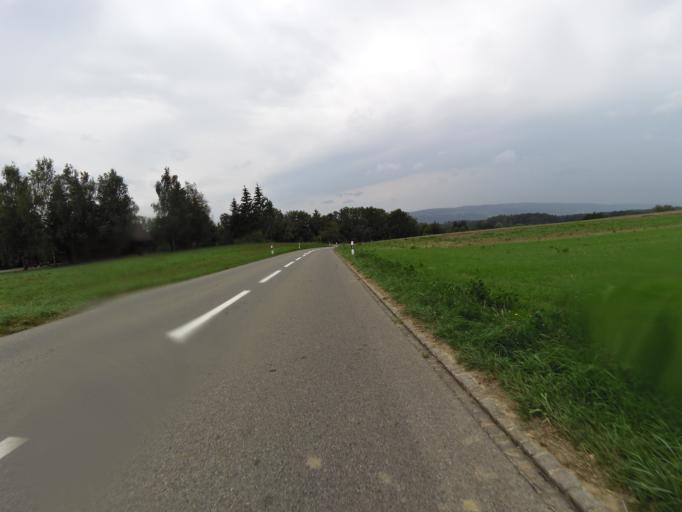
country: CH
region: Thurgau
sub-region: Weinfelden District
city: Wigoltingen
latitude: 47.6153
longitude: 9.0419
